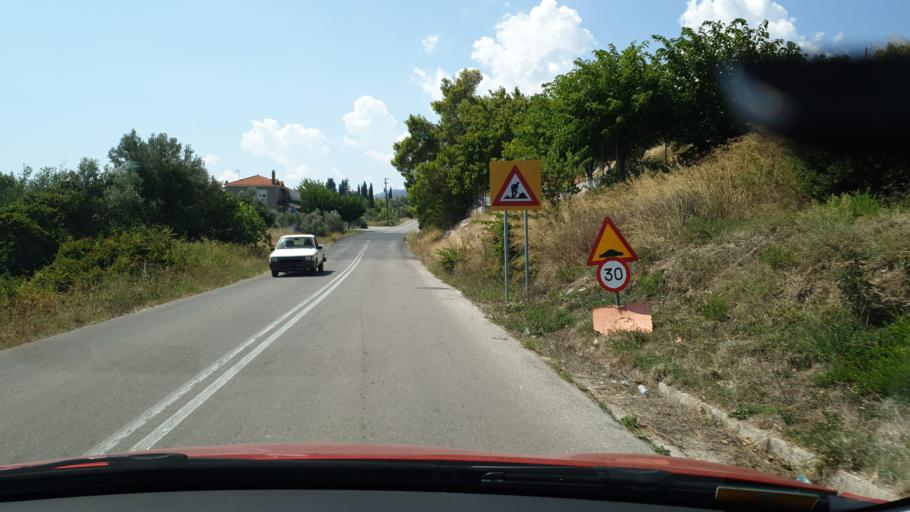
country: GR
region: Central Greece
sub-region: Nomos Evvoias
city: Oxilithos
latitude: 38.5856
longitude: 24.0658
